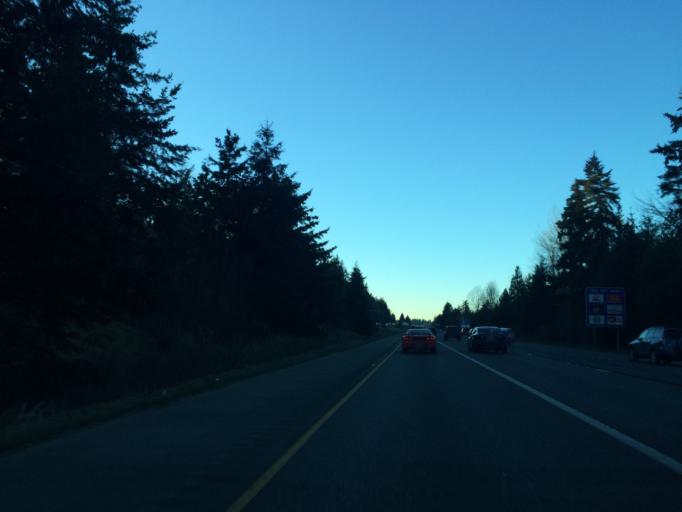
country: US
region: Washington
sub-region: King County
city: West Lake Sammamish
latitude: 47.5715
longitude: -122.1133
